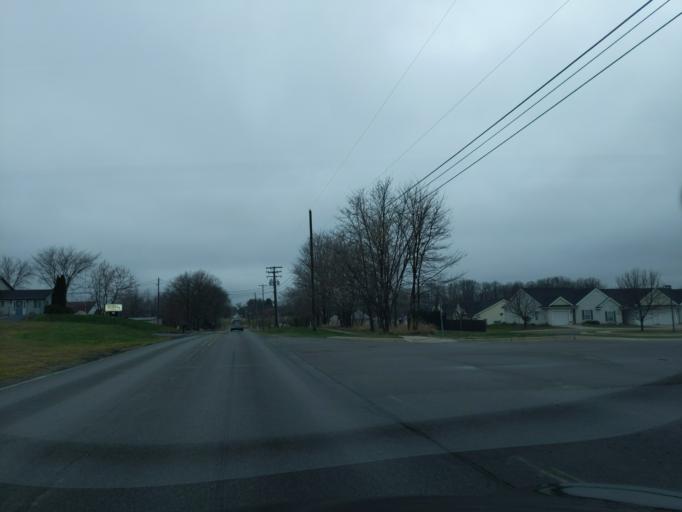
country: US
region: Michigan
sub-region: Jackson County
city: Jackson
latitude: 42.2766
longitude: -84.4581
